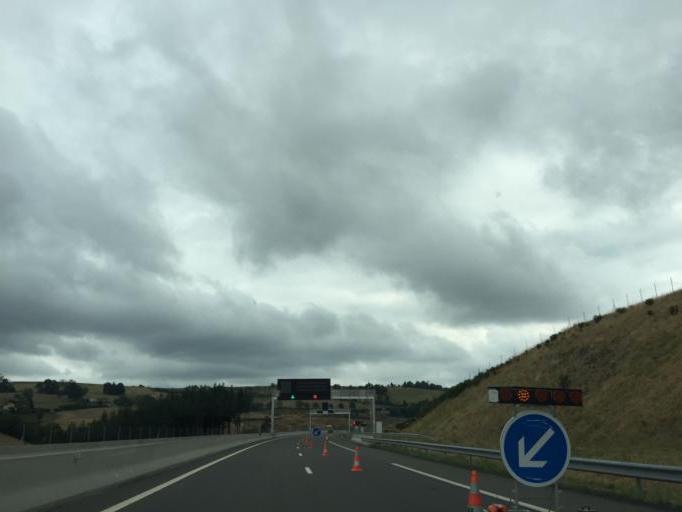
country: FR
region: Rhone-Alpes
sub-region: Departement de la Loire
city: Violay
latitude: 45.8619
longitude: 4.3172
